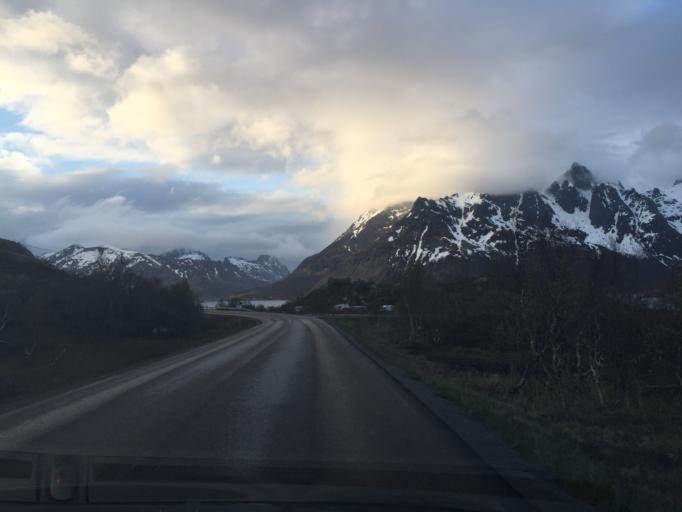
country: NO
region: Nordland
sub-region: Vagan
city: Svolvaer
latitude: 68.3142
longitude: 14.7133
